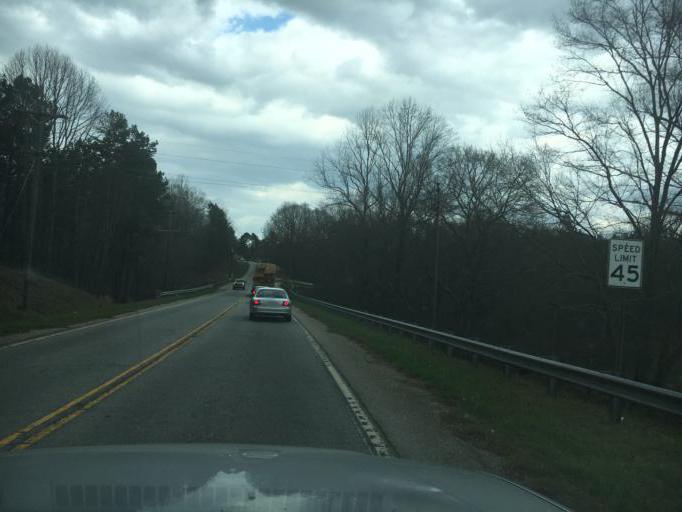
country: US
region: South Carolina
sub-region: Oconee County
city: Walhalla
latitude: 34.7654
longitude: -83.0348
